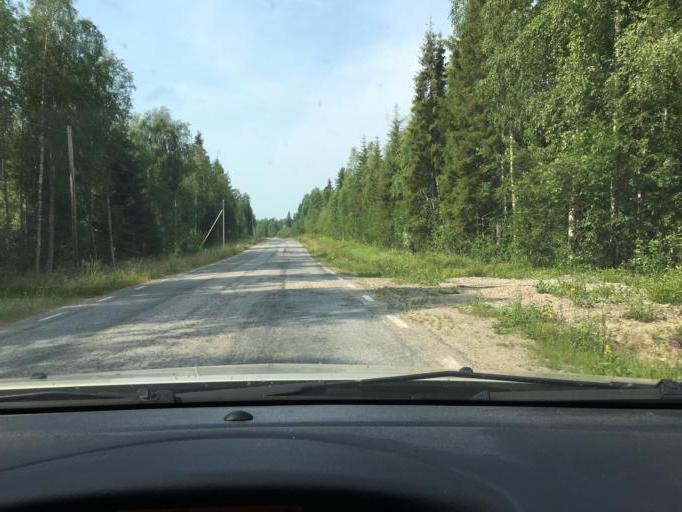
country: SE
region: Norrbotten
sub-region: Kalix Kommun
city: Rolfs
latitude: 65.7741
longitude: 22.9971
